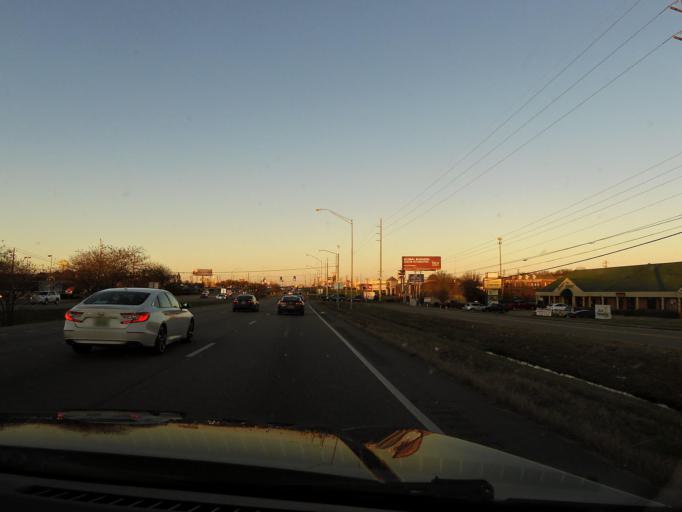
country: US
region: Alabama
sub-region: Montgomery County
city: Montgomery
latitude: 32.3500
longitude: -86.2206
